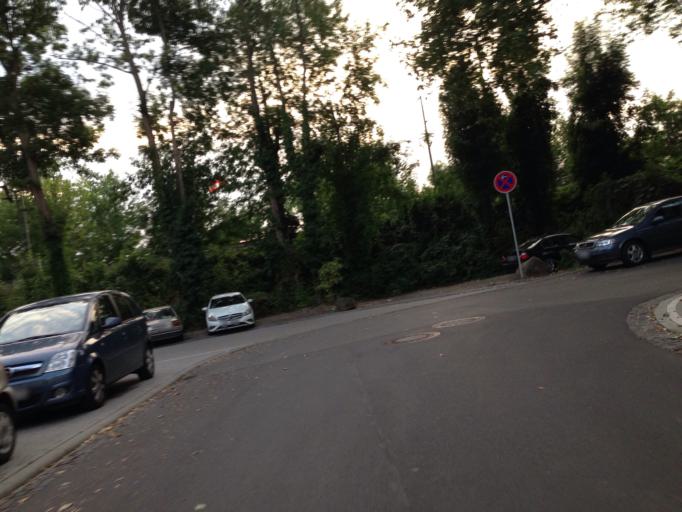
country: DE
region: Hesse
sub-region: Regierungsbezirk Giessen
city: Giessen
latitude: 50.5899
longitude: 8.6707
